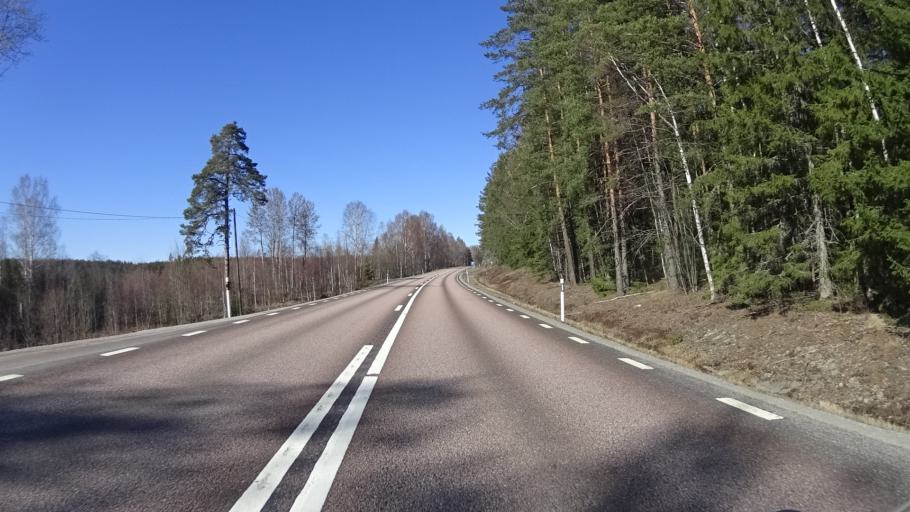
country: SE
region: Vaermland
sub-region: Sunne Kommun
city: Sunne
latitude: 59.6437
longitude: 12.9445
